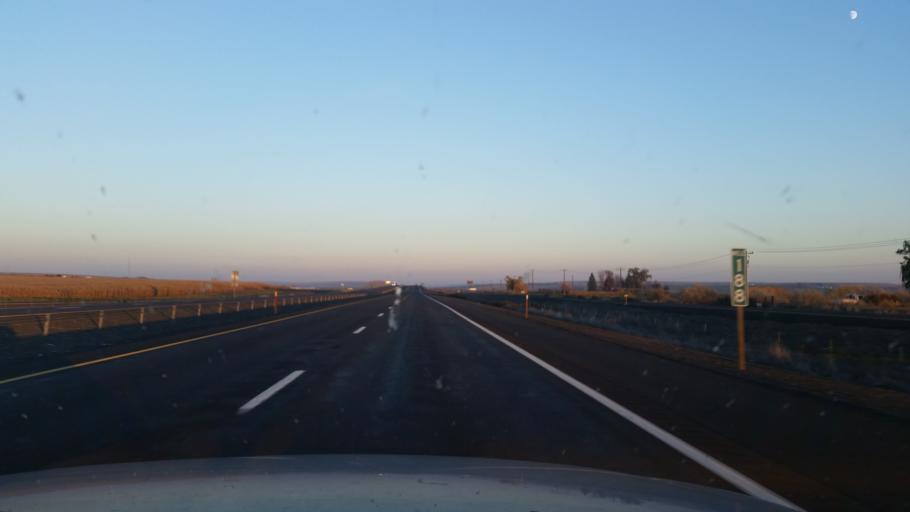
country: US
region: Washington
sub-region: Grant County
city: Warden
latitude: 47.0861
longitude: -119.0642
